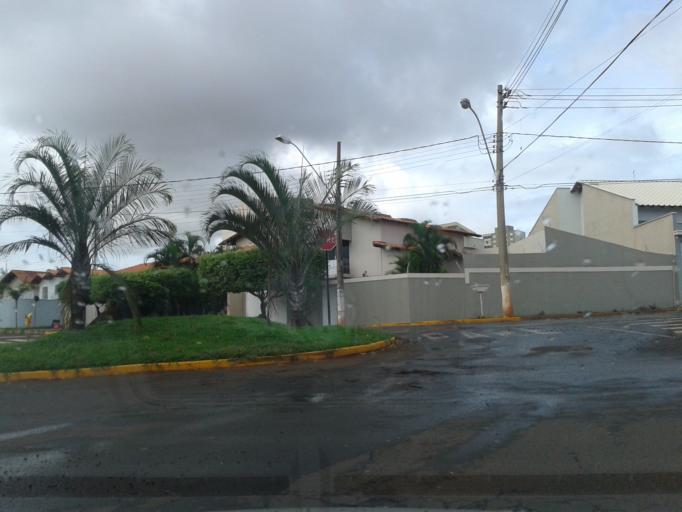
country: BR
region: Minas Gerais
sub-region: Ituiutaba
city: Ituiutaba
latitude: -18.9655
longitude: -49.4623
